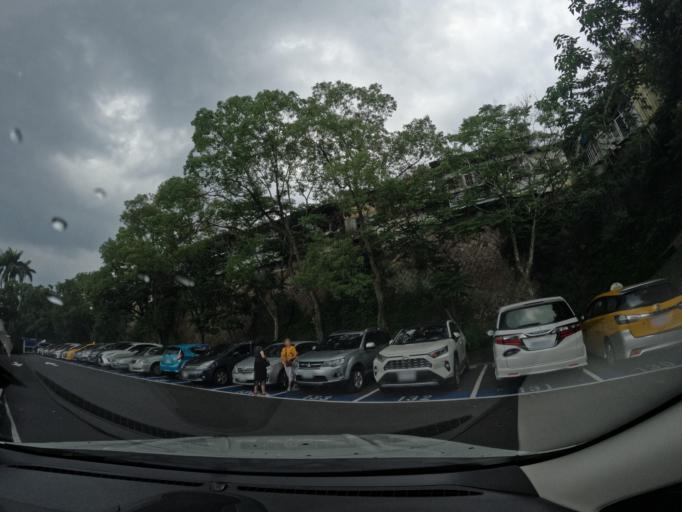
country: TW
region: Taiwan
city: Daxi
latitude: 24.9051
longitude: 121.4006
